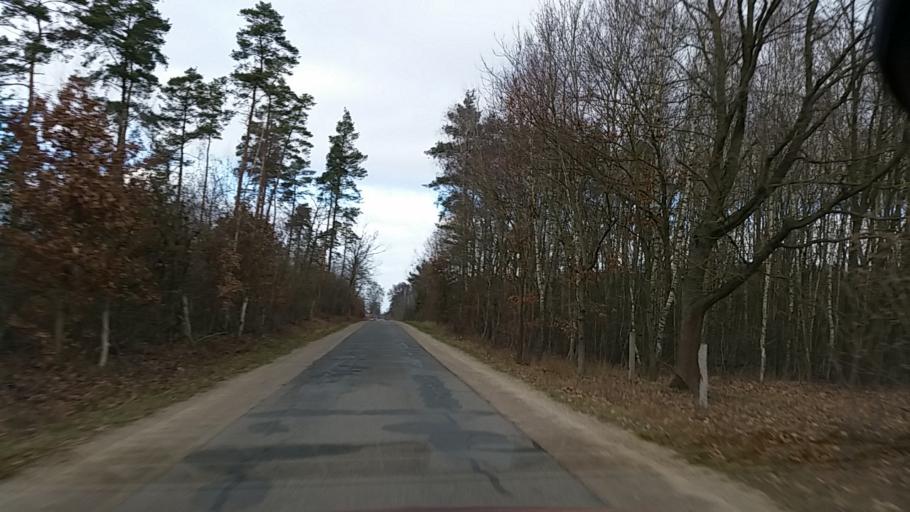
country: DE
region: Lower Saxony
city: Wieren
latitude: 52.8701
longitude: 10.6603
